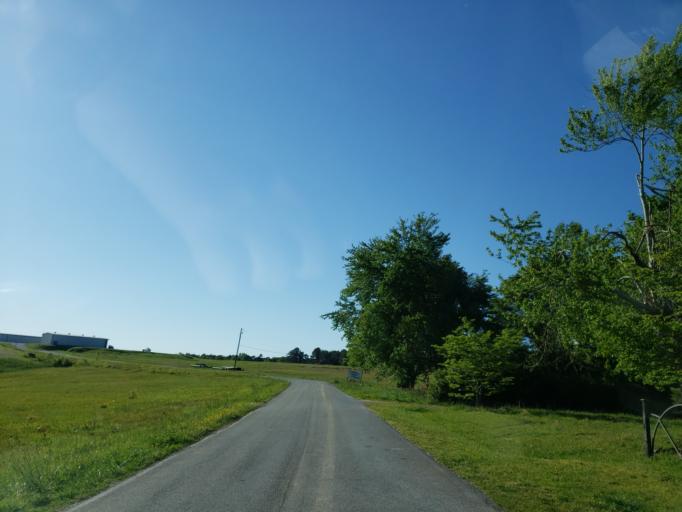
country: US
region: Georgia
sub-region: Polk County
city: Aragon
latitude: 34.0169
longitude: -85.1463
